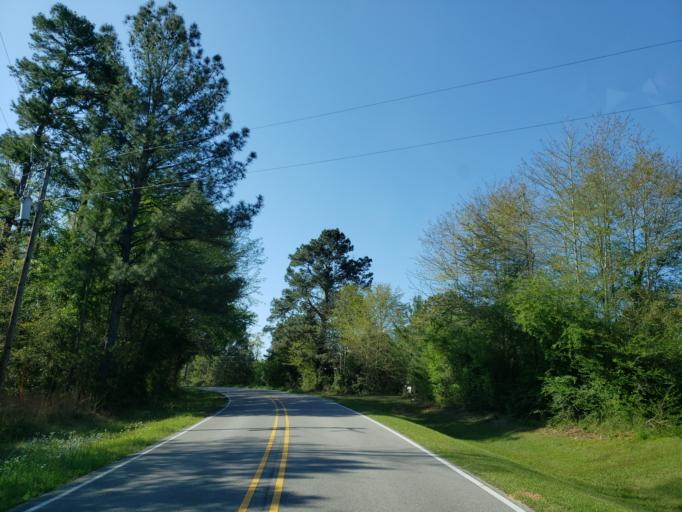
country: US
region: Mississippi
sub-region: Covington County
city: Collins
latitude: 31.6117
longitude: -89.3821
